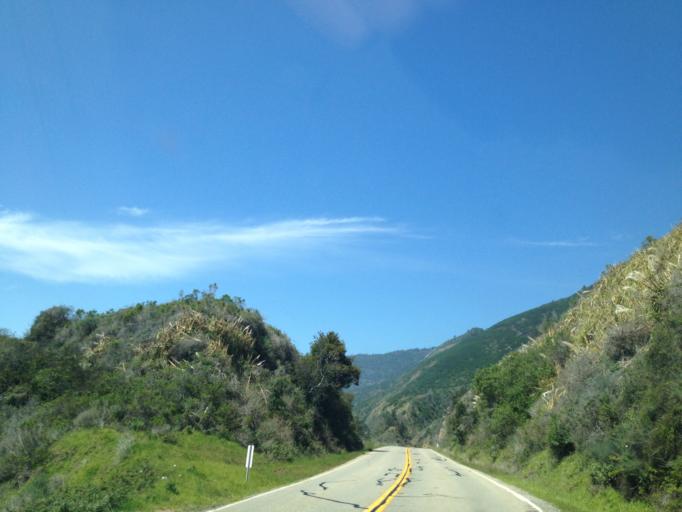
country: US
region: California
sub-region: Monterey County
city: Greenfield
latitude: 35.9965
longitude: -121.4982
